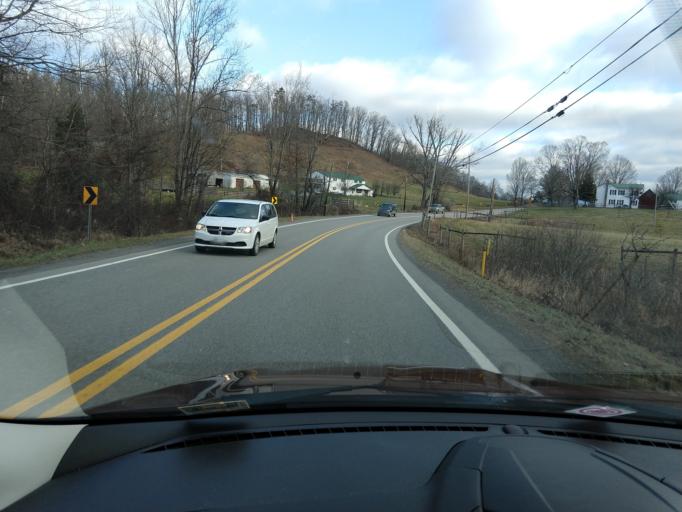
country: US
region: West Virginia
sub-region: Randolph County
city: Elkins
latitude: 38.7800
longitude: -79.9142
